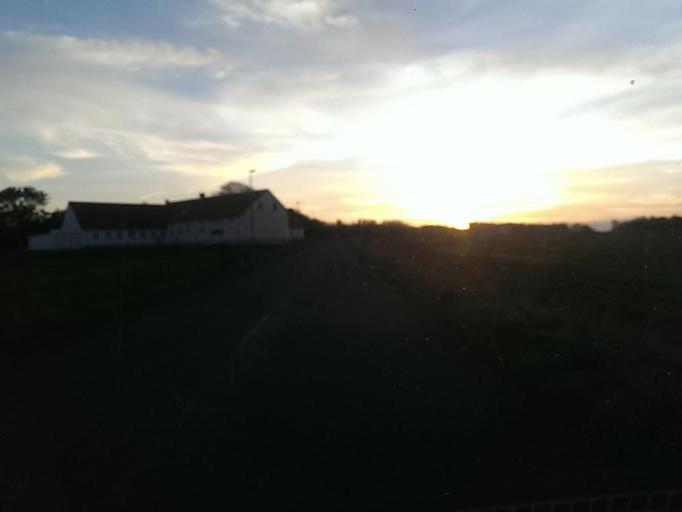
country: DK
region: South Denmark
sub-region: Esbjerg Kommune
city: Tjaereborg
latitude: 55.4659
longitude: 8.5951
